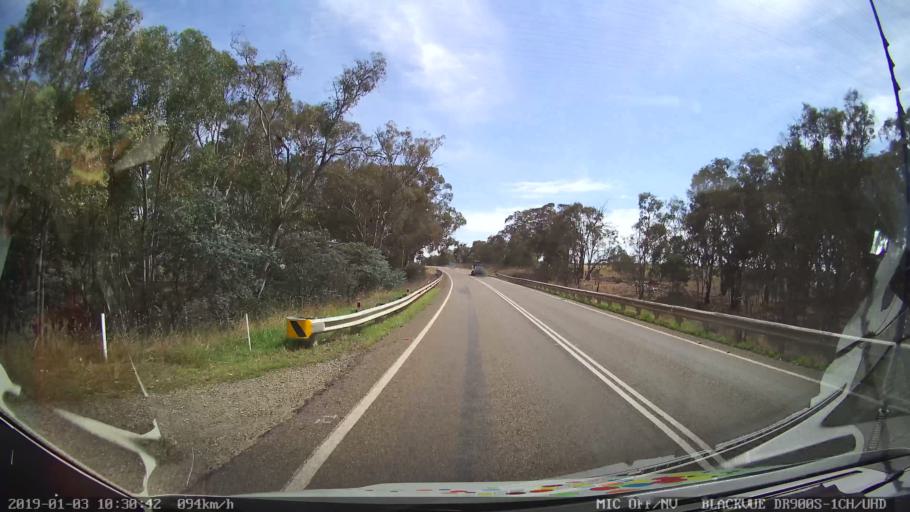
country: AU
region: New South Wales
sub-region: Young
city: Young
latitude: -34.3593
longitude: 148.2710
